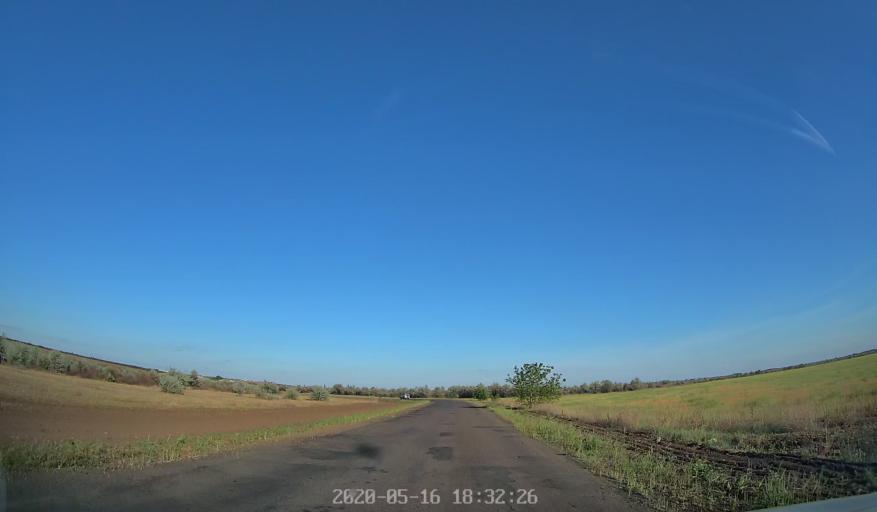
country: UA
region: Odessa
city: Lymanske
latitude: 46.5371
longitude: 30.0537
